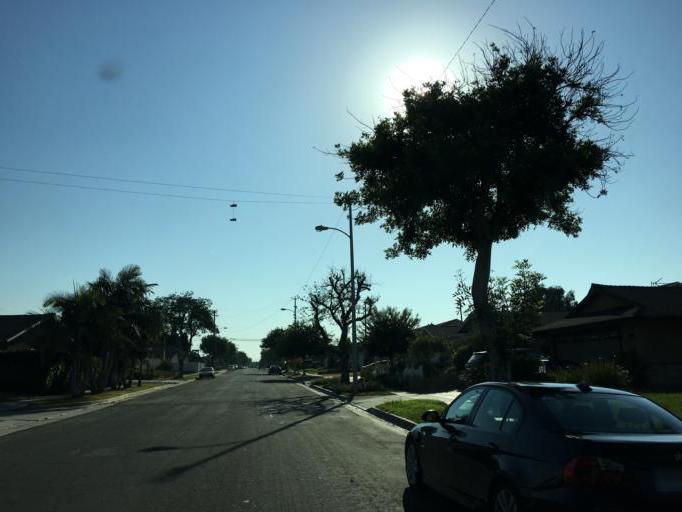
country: US
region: California
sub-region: Los Angeles County
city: Avocado Heights
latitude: 34.0358
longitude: -118.0126
